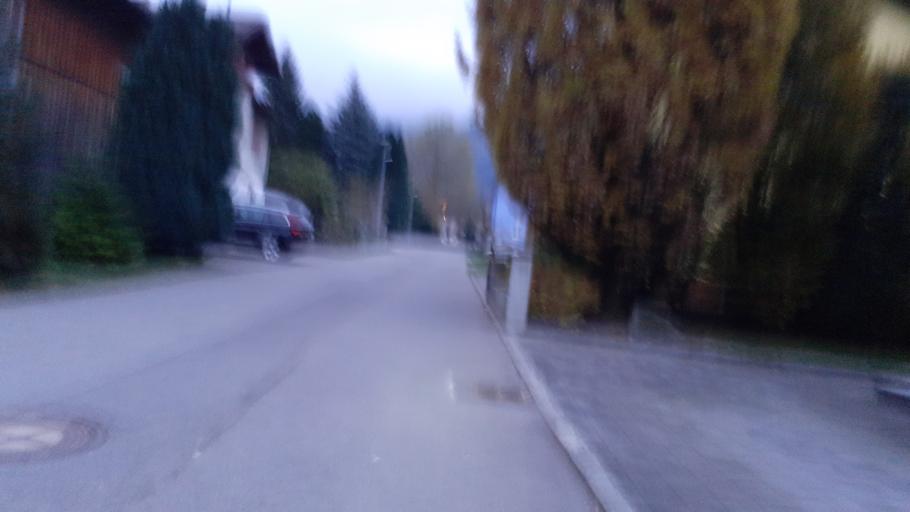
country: AT
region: Vorarlberg
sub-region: Politischer Bezirk Feldkirch
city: Gotzis
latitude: 47.3384
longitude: 9.6364
